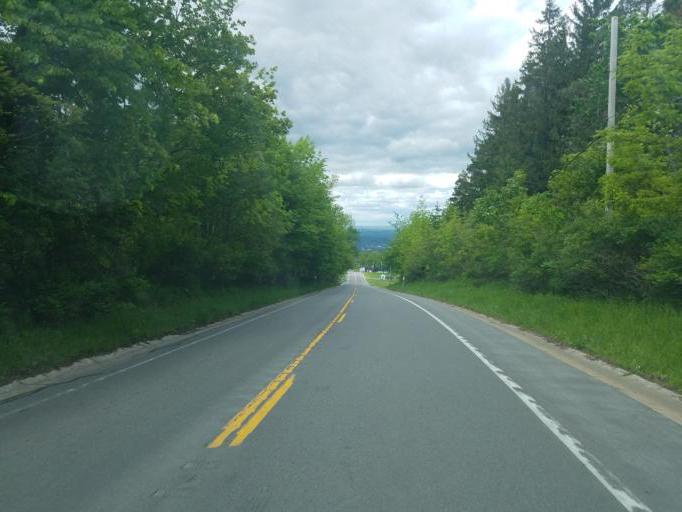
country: US
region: New York
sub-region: Herkimer County
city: Mohawk
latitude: 42.9747
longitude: -75.0116
